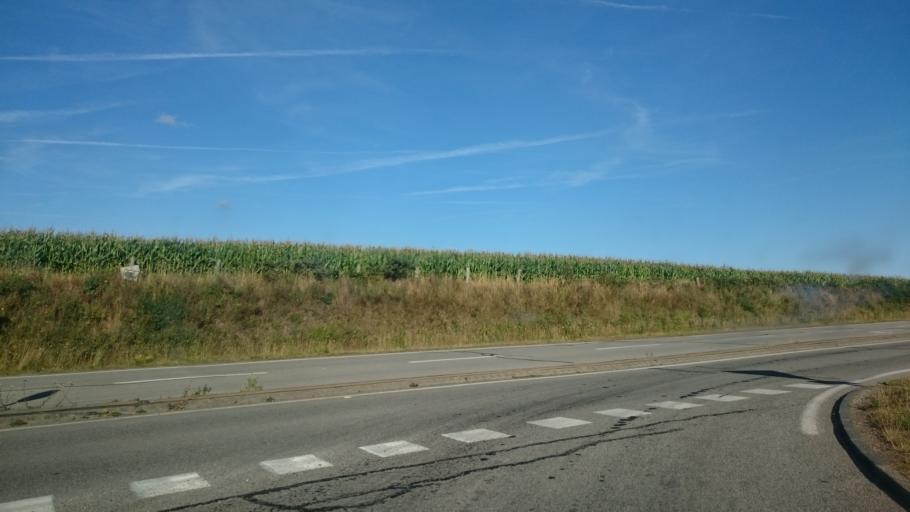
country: FR
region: Lower Normandy
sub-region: Departement de la Manche
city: Martinvast
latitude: 49.5757
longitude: -1.7051
